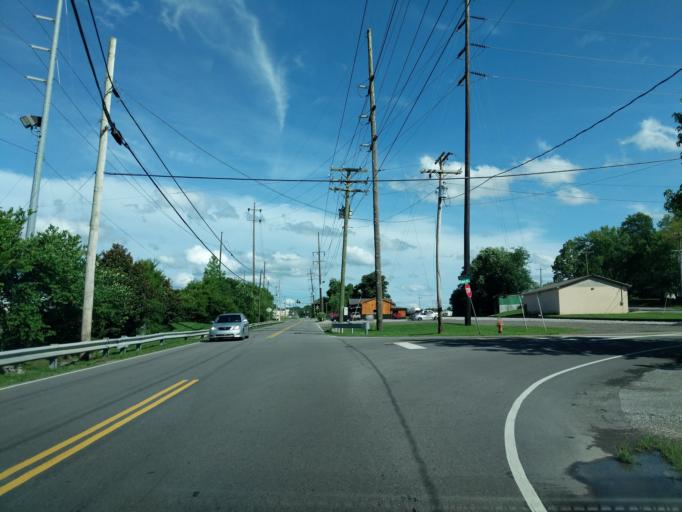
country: US
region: Tennessee
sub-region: Davidson County
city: Lakewood
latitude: 36.2729
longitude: -86.6642
